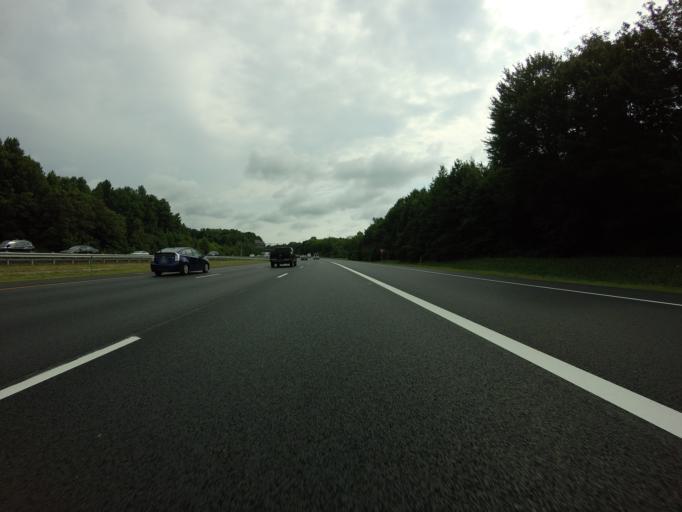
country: US
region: Maryland
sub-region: Harford County
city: Aberdeen
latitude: 39.5306
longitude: -76.1817
